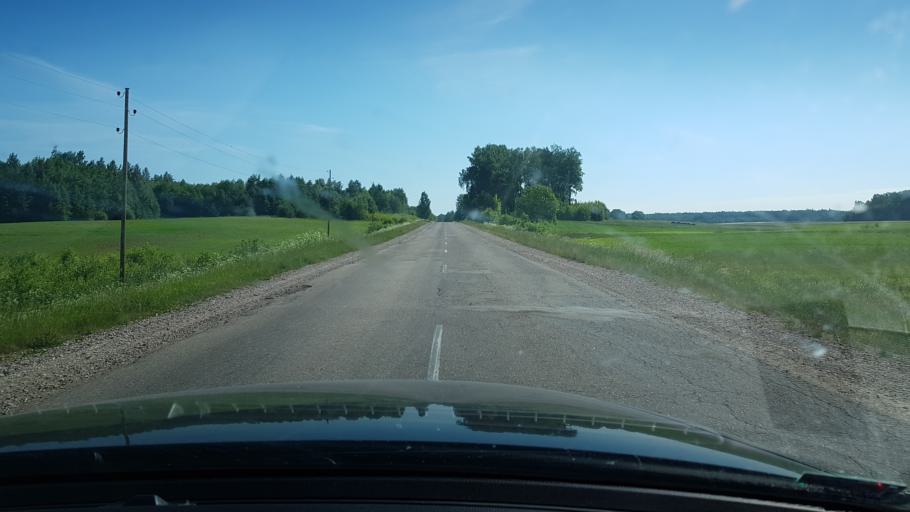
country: LV
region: Daugavpils
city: Daugavpils
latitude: 55.8143
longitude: 26.7231
